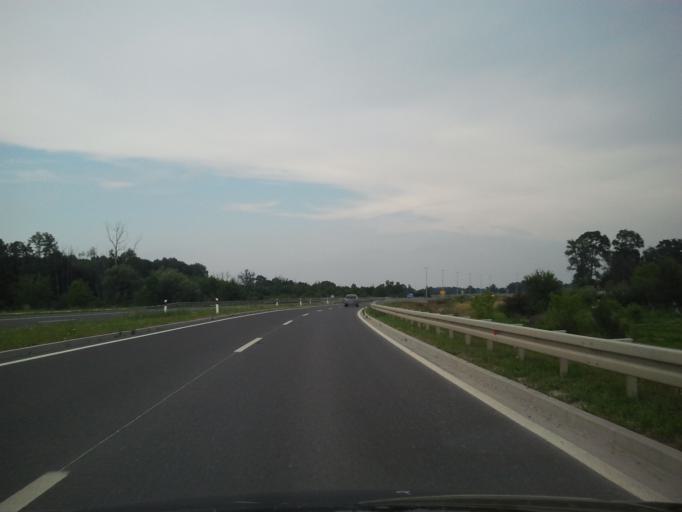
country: HR
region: Zagrebacka
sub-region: Grad Velika Gorica
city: Velika Gorica
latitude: 45.7320
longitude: 16.0977
